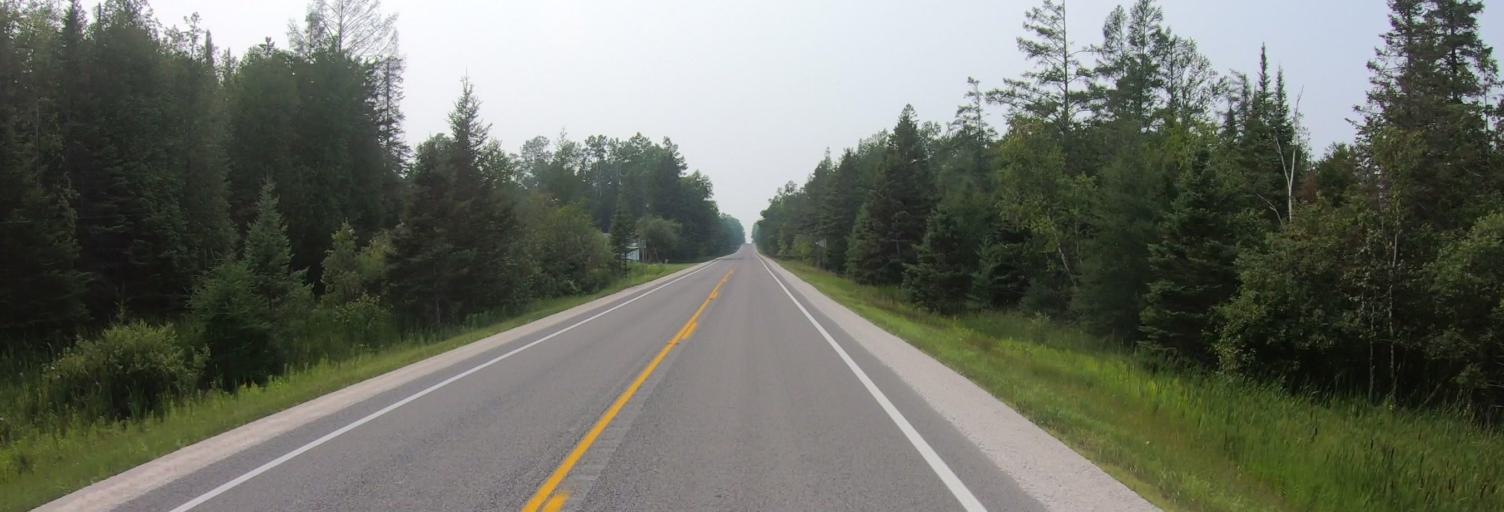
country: US
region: Michigan
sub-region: Chippewa County
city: Sault Ste. Marie
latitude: 46.0723
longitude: -84.1219
